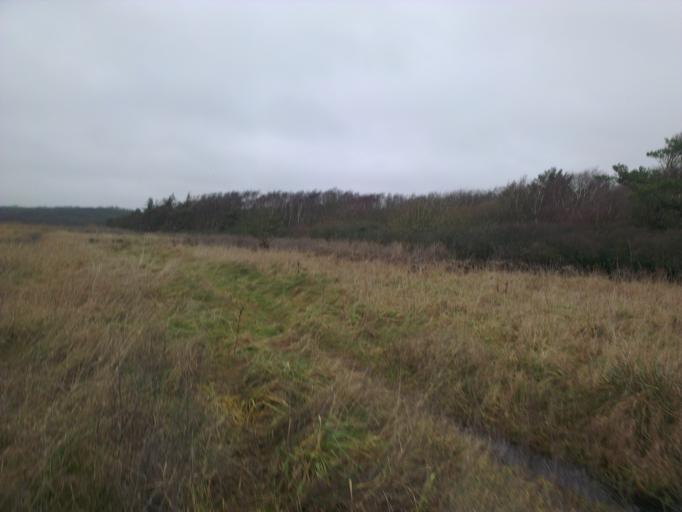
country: DK
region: Capital Region
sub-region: Frederikssund Kommune
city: Jaegerspris
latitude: 55.8474
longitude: 11.9598
